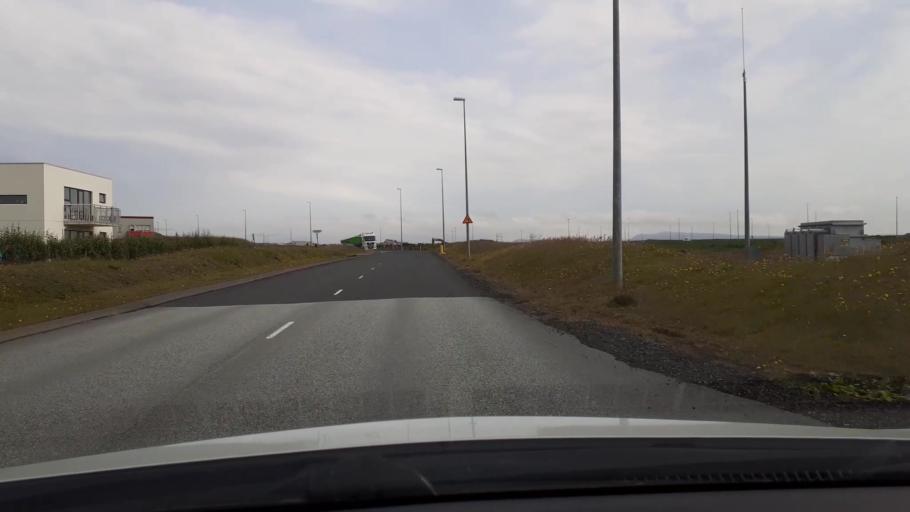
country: IS
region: Southern Peninsula
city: Reykjanesbaer
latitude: 63.9709
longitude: -22.5177
